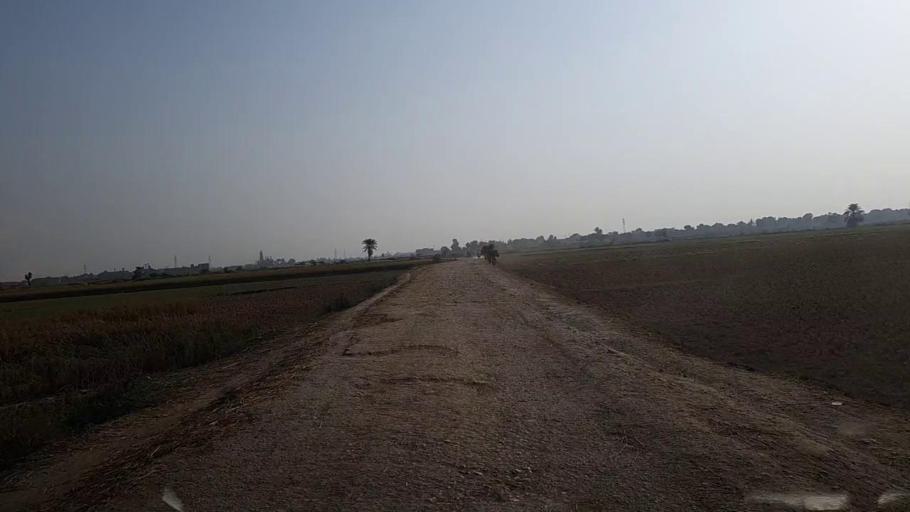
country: PK
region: Sindh
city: Kandhkot
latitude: 28.2834
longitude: 69.2567
